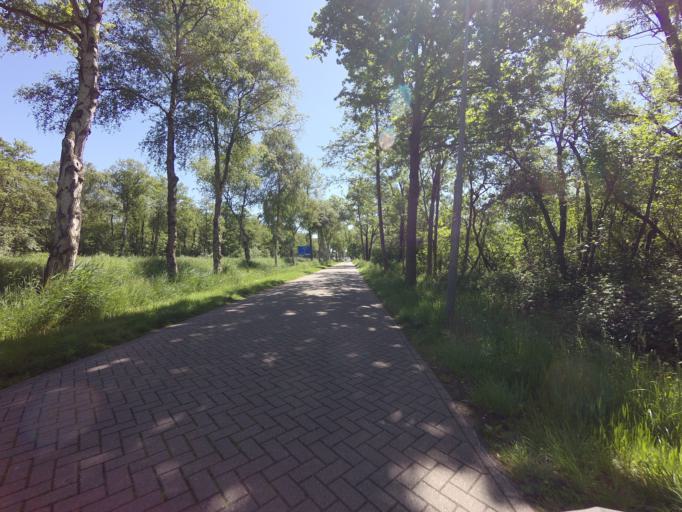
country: NL
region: North Holland
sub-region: Gemeente Wijdemeren
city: Oud-Loosdrecht
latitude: 52.2279
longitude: 5.0789
